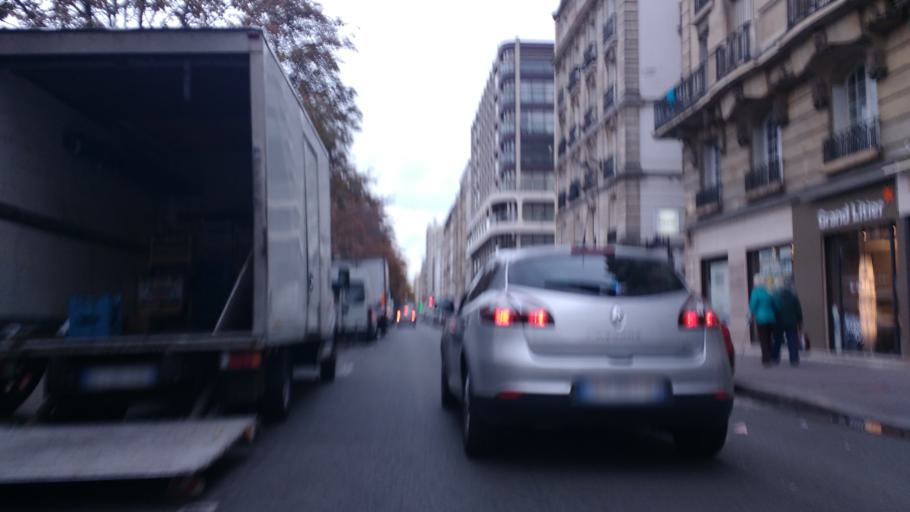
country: FR
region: Ile-de-France
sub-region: Departement du Val-de-Marne
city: Saint-Mande
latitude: 48.8474
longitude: 2.4038
